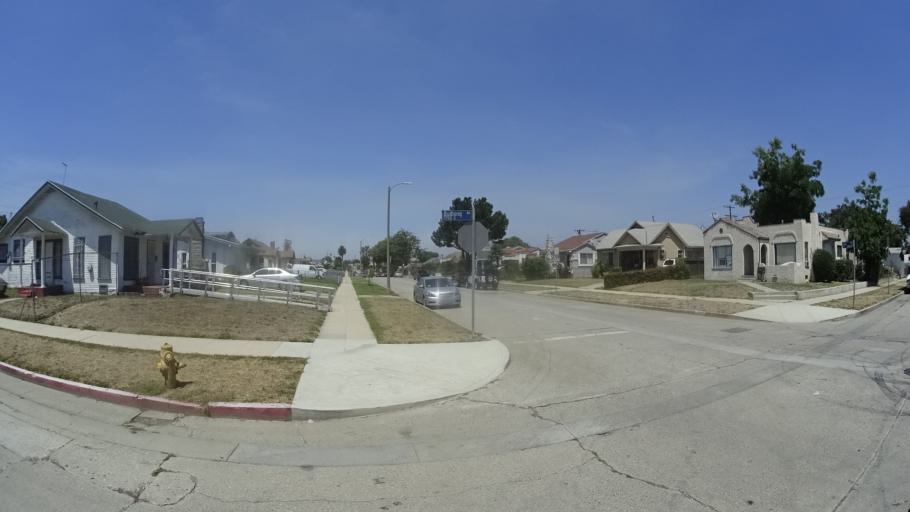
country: US
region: California
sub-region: Los Angeles County
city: Westmont
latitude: 33.9701
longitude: -118.2961
